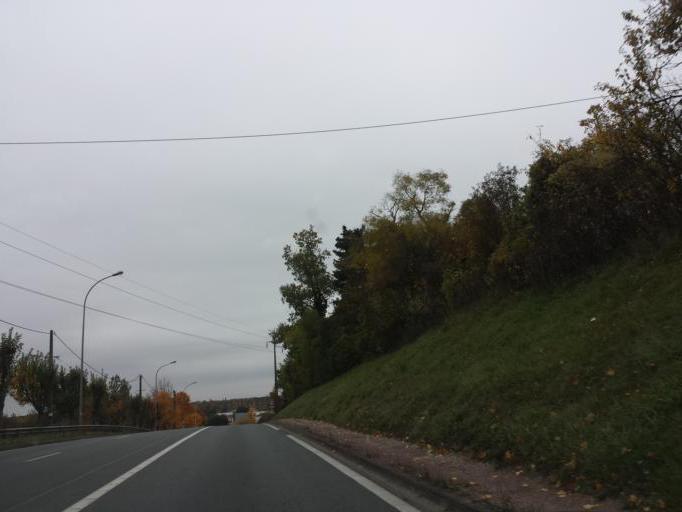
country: FR
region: Poitou-Charentes
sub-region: Departement de la Charente
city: Angouleme
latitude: 45.6325
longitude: 0.1320
